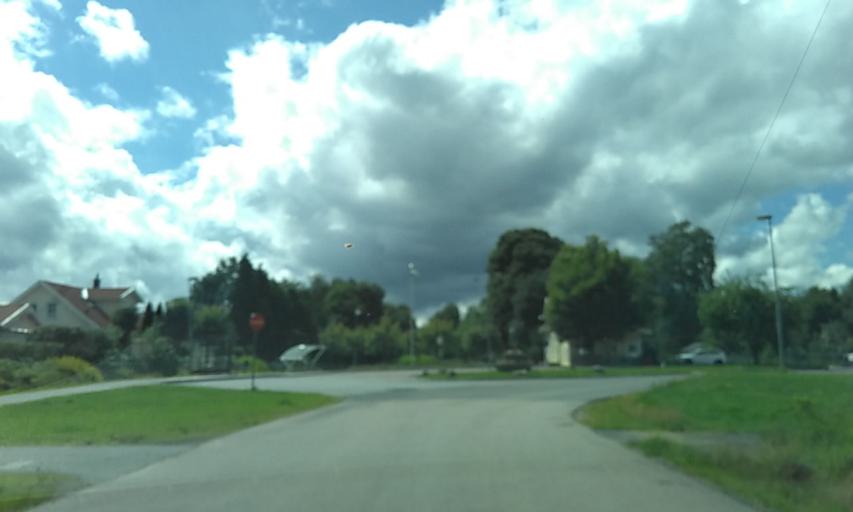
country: SE
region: Vaestra Goetaland
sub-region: Lerums Kommun
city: Grabo
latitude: 57.9150
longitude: 12.3701
